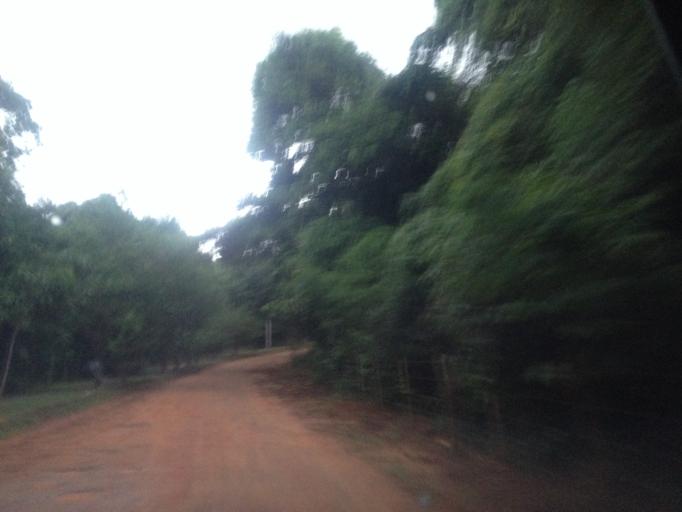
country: BR
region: Bahia
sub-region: Mata De Sao Joao
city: Mata de Sao Joao
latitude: -12.5726
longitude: -38.0238
